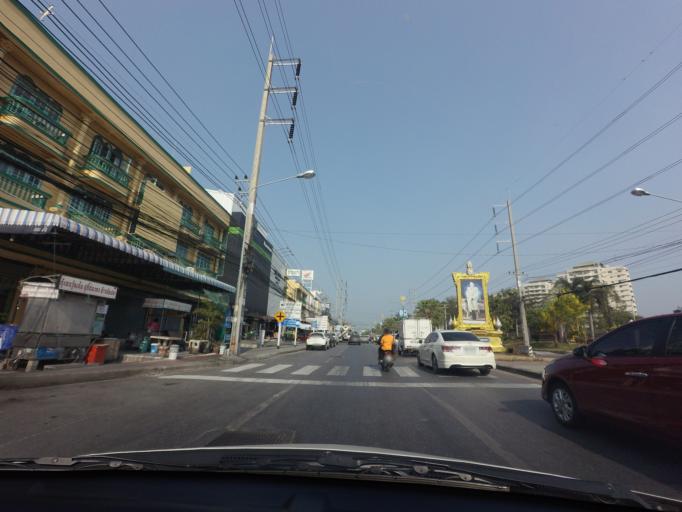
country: TH
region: Nakhon Pathom
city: Salaya
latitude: 13.8015
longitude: 100.3187
